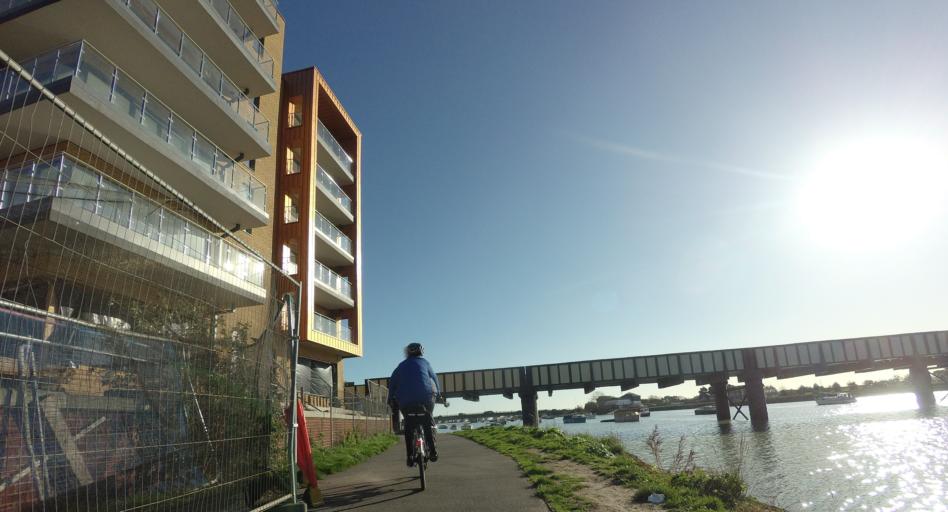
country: GB
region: England
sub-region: West Sussex
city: Shoreham-by-Sea
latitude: 50.8347
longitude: -0.2821
